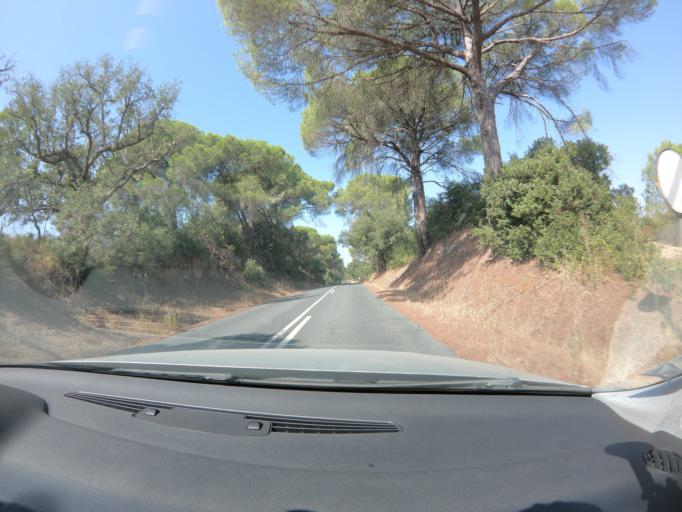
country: PT
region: Setubal
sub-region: Alcacer do Sal
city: Alcacer do Sal
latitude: 38.3042
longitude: -8.4183
